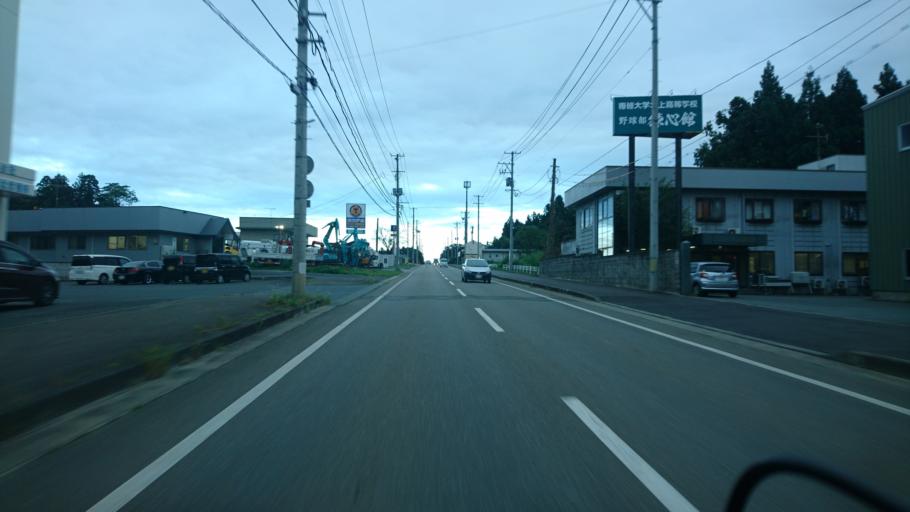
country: JP
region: Iwate
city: Kitakami
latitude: 39.3099
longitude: 141.1029
